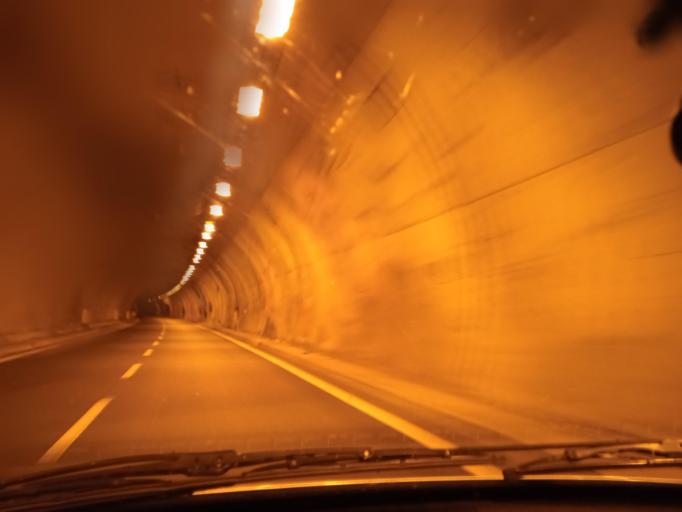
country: IT
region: Sicily
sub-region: Messina
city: Santo Stefano di Camastra
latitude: 38.0047
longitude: 14.3495
